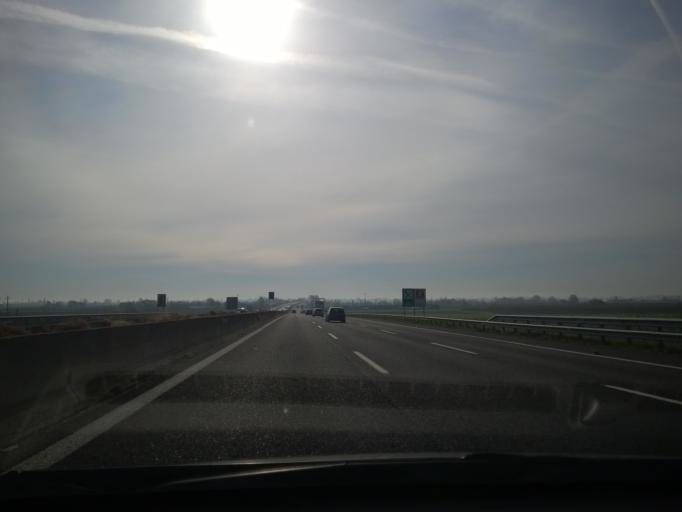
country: IT
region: Emilia-Romagna
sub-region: Provincia di Ravenna
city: Solarolo
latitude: 44.3497
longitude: 11.8290
